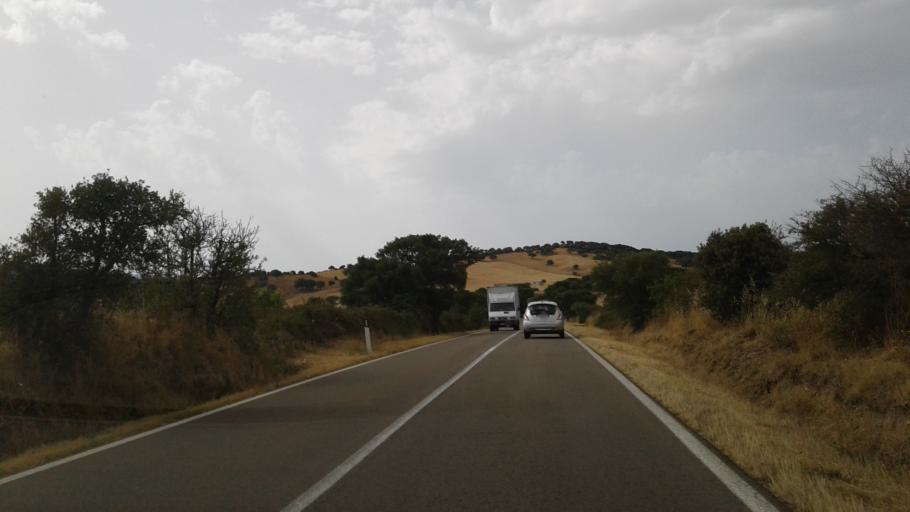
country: IT
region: Sardinia
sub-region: Provincia di Olbia-Tempio
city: Sant'Antonio di Gallura
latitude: 40.9490
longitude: 9.2969
